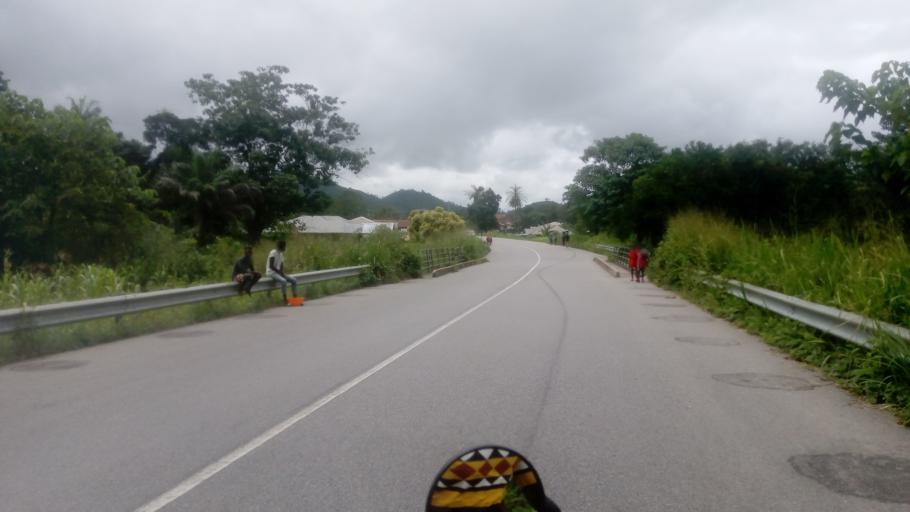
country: SL
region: Northern Province
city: Makali
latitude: 8.6305
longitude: -11.6651
